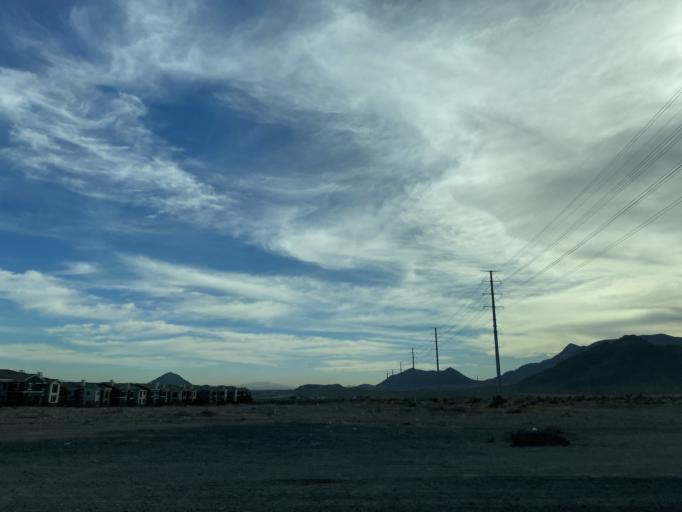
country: US
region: Nevada
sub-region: Clark County
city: Summerlin South
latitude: 36.2772
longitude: -115.3331
